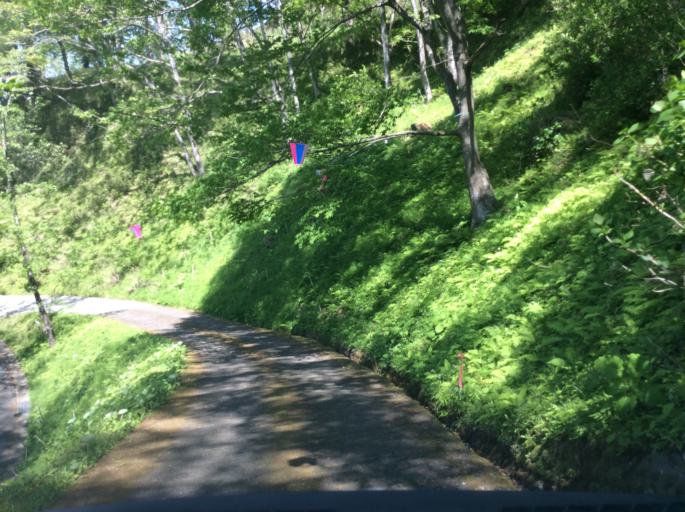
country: JP
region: Fukushima
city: Miharu
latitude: 37.4426
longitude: 140.4955
